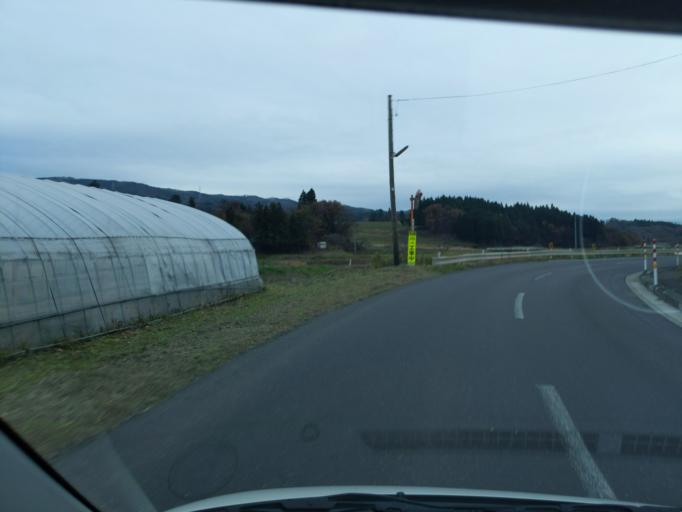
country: JP
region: Iwate
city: Kitakami
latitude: 39.2818
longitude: 141.2668
